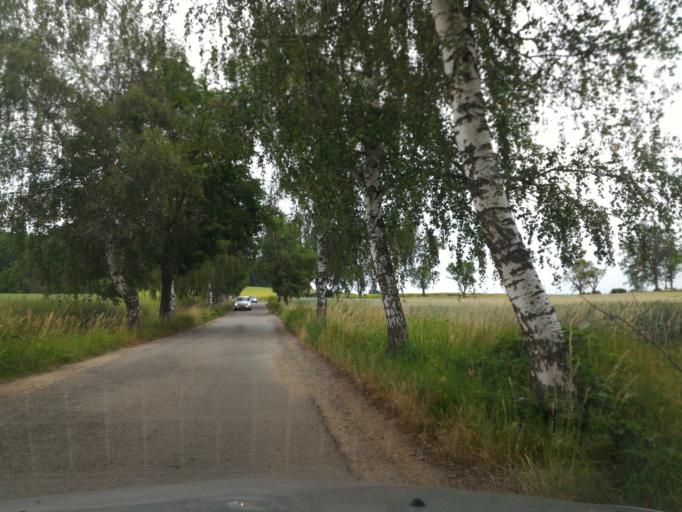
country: CZ
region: Vysocina
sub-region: Okres Jihlava
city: Telc
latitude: 49.1754
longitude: 15.4661
